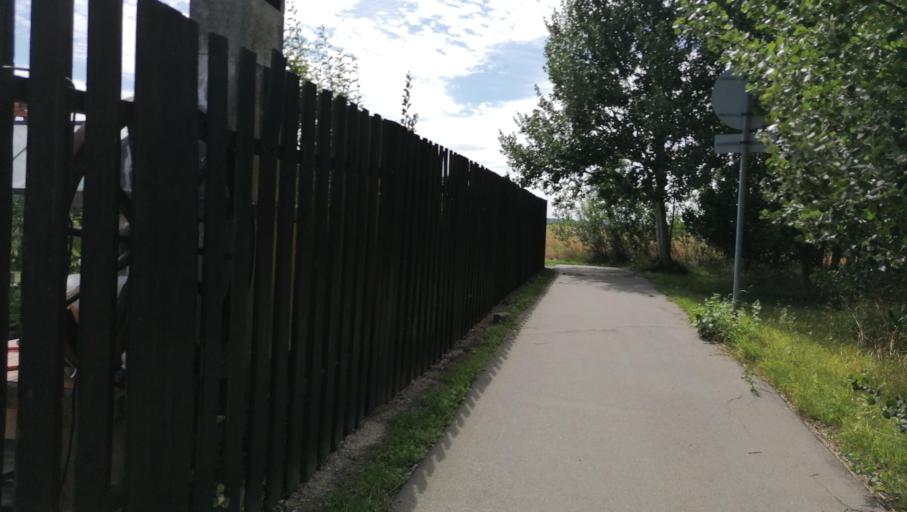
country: DK
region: Zealand
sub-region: Odsherred Kommune
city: Horve
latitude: 55.7847
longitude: 11.4593
